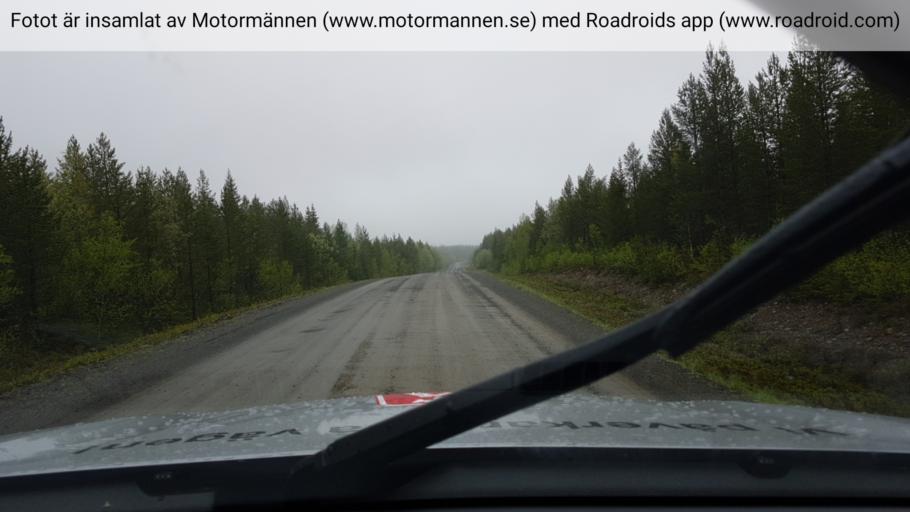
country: SE
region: Jaemtland
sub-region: Krokoms Kommun
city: Valla
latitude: 63.0652
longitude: 13.9593
